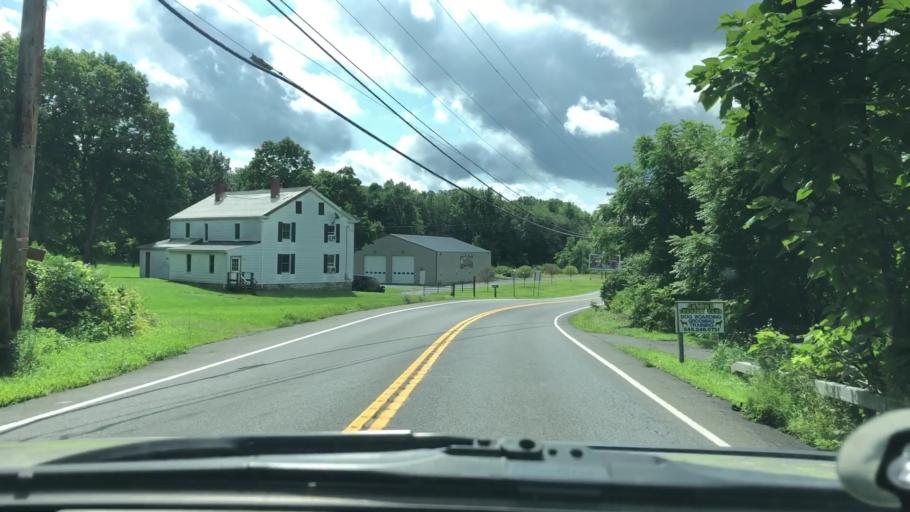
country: US
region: New York
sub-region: Ulster County
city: Manorville
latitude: 42.1282
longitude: -73.9967
